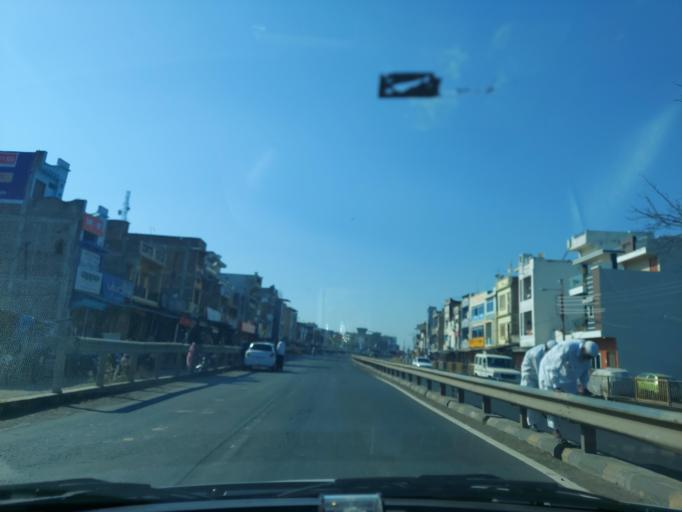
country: IN
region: Madhya Pradesh
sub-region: Dhar
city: Dhar
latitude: 22.7965
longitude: 75.2854
